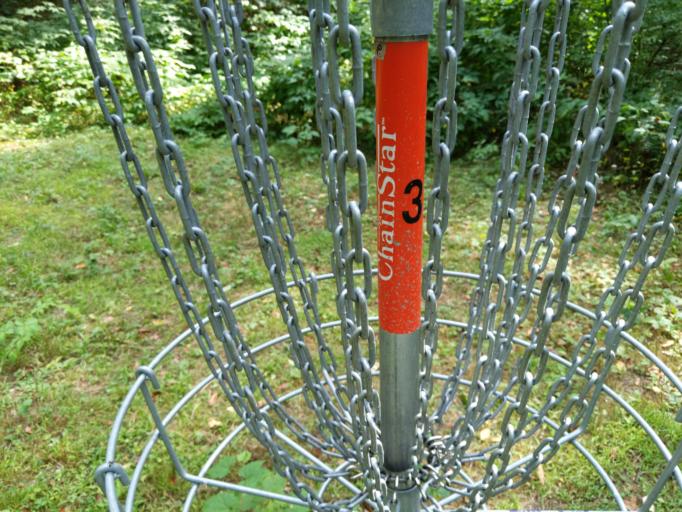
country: US
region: Michigan
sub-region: Ionia County
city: Ionia
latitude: 42.9708
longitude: -85.1222
